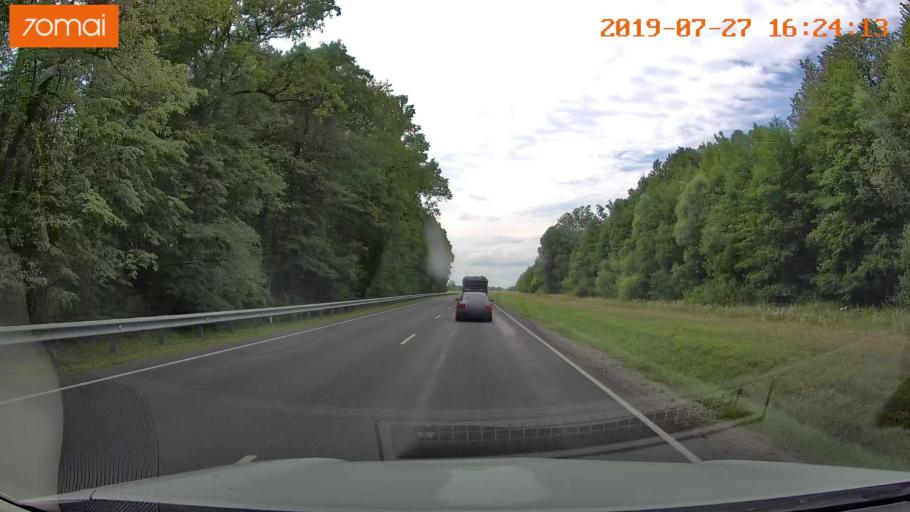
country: RU
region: Kaliningrad
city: Zheleznodorozhnyy
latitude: 54.6334
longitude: 21.4571
